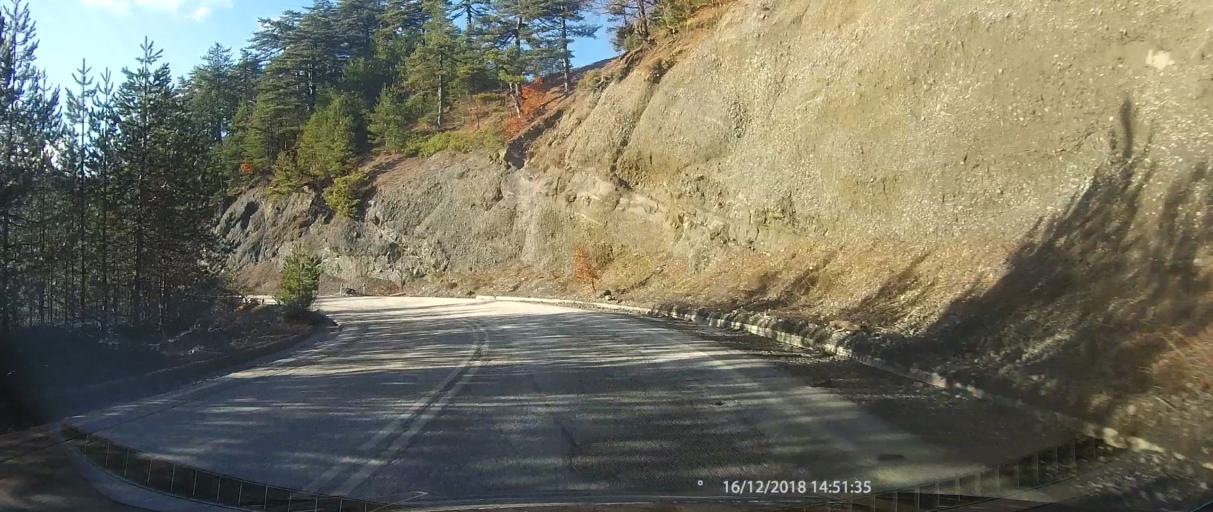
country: GR
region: West Macedonia
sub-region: Nomos Kastorias
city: Nestorio
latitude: 40.2043
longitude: 21.0711
